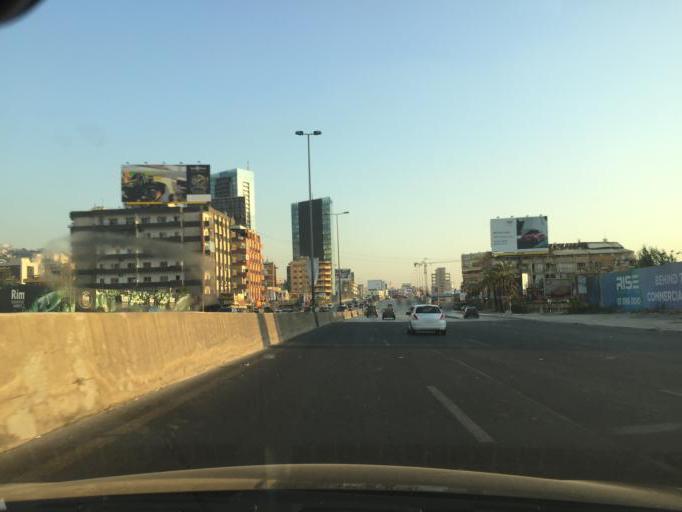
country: LB
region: Mont-Liban
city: Jdaidet el Matn
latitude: 33.9210
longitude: 35.5856
